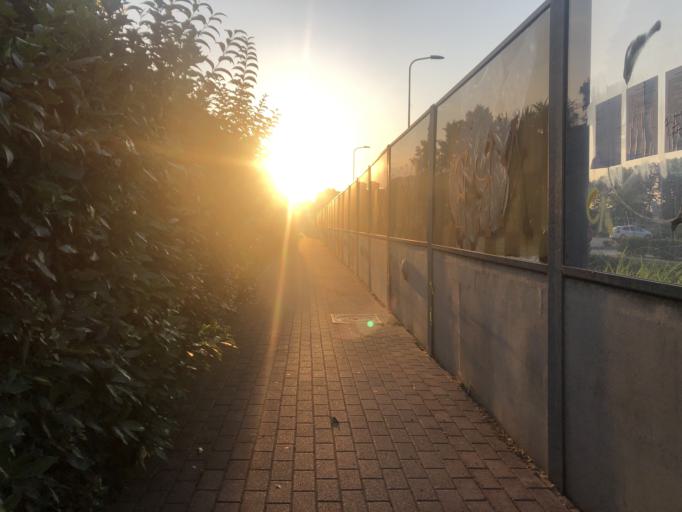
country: IT
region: Tuscany
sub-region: Province of Pisa
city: Pisa
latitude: 43.7235
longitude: 10.4131
